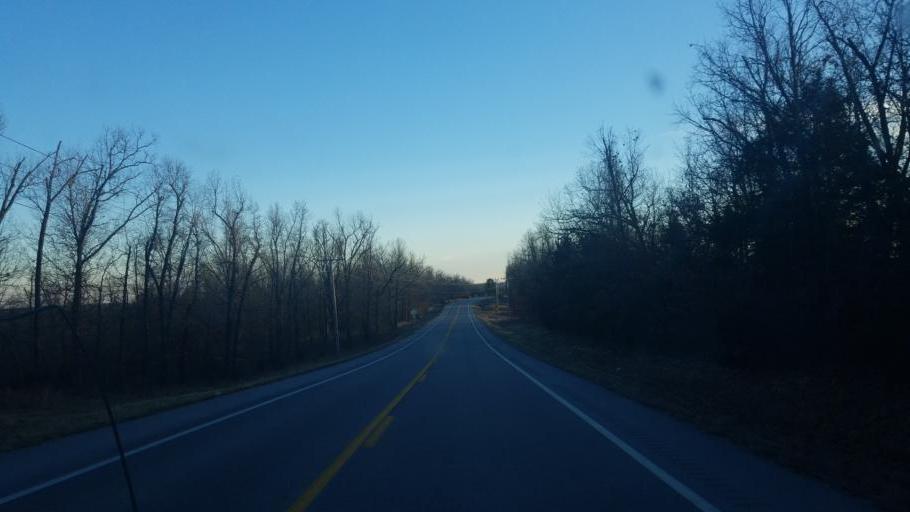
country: US
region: Arkansas
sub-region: Baxter County
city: Mountain Home
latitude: 36.3829
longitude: -92.1528
